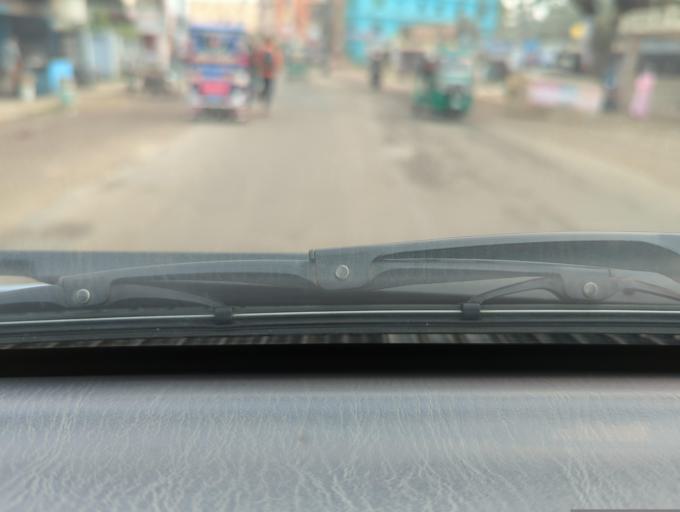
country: BD
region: Sylhet
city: Maulavi Bazar
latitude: 24.4892
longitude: 91.7483
